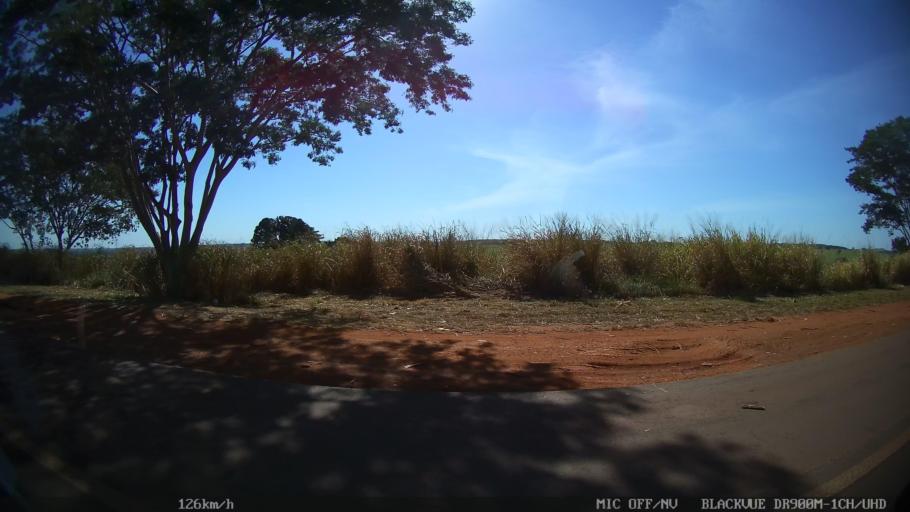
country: BR
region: Sao Paulo
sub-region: Olimpia
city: Olimpia
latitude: -20.6812
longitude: -48.8970
